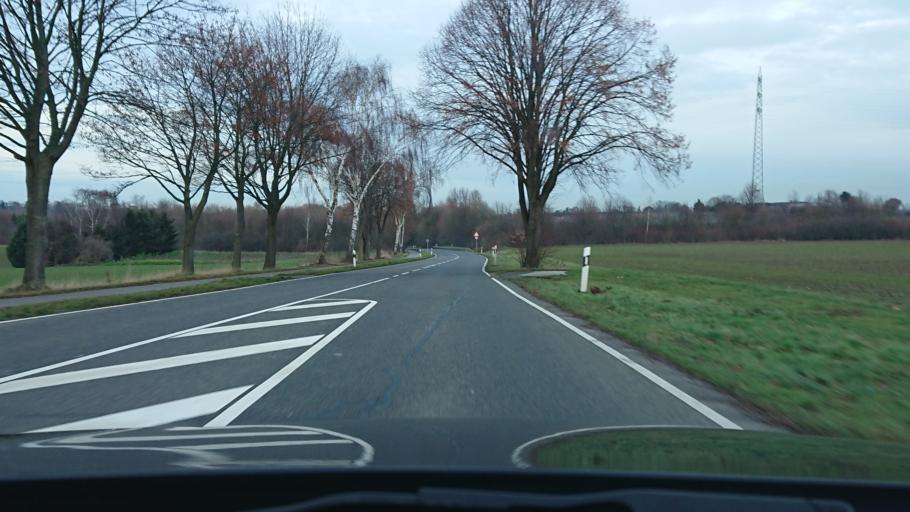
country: DE
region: North Rhine-Westphalia
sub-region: Regierungsbezirk Koln
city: Pulheim
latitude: 51.0087
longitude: 6.7497
